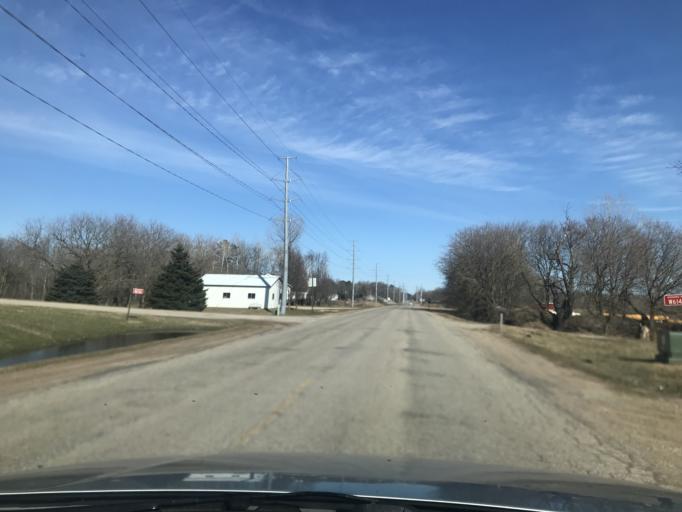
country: US
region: Michigan
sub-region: Menominee County
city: Menominee
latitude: 45.1446
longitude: -87.6356
